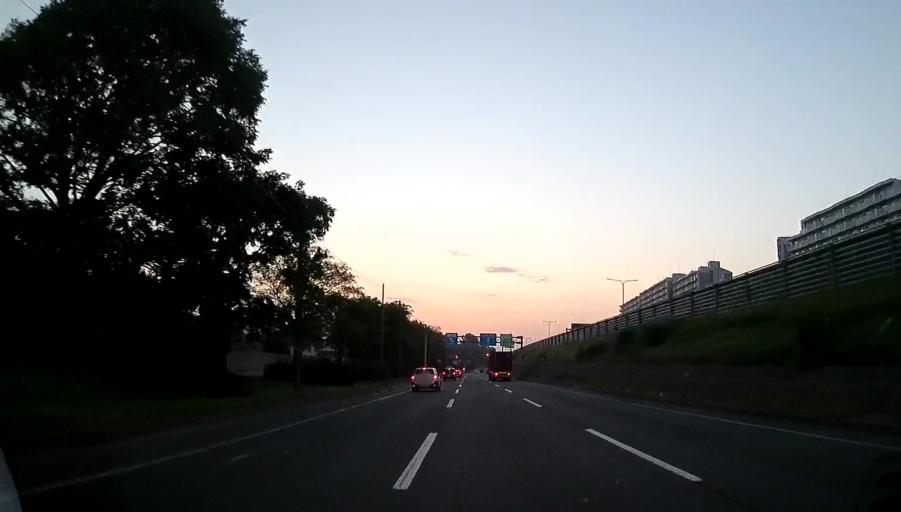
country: JP
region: Hokkaido
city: Sapporo
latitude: 43.0237
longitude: 141.4547
